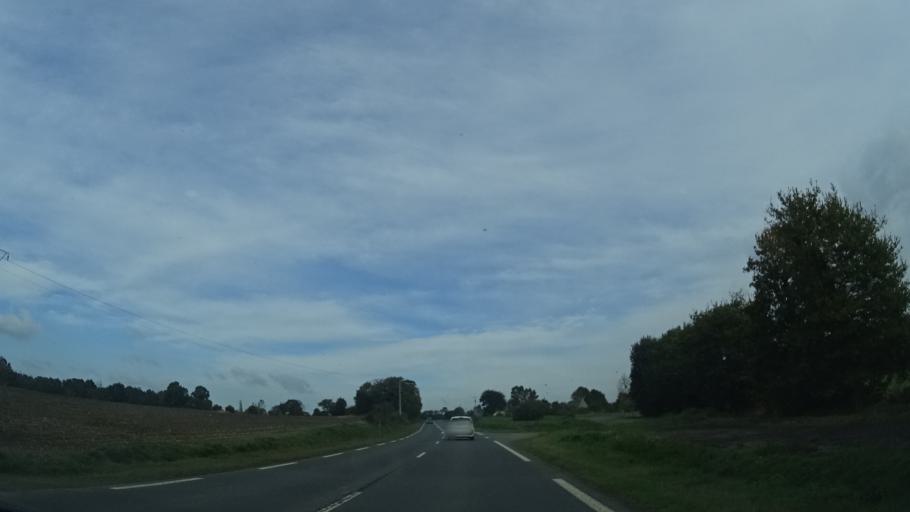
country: FR
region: Brittany
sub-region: Departement d'Ille-et-Vilaine
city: Quebriac
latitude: 48.3580
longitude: -1.7719
